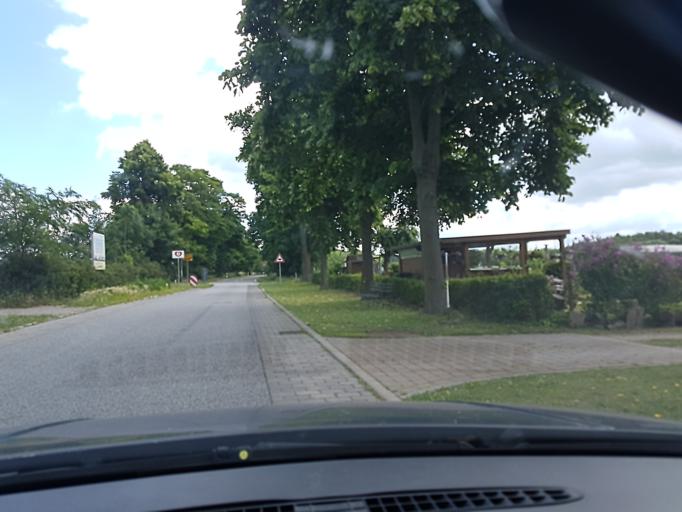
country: DE
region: Brandenburg
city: Neuruppin
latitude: 52.8585
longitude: 12.8761
